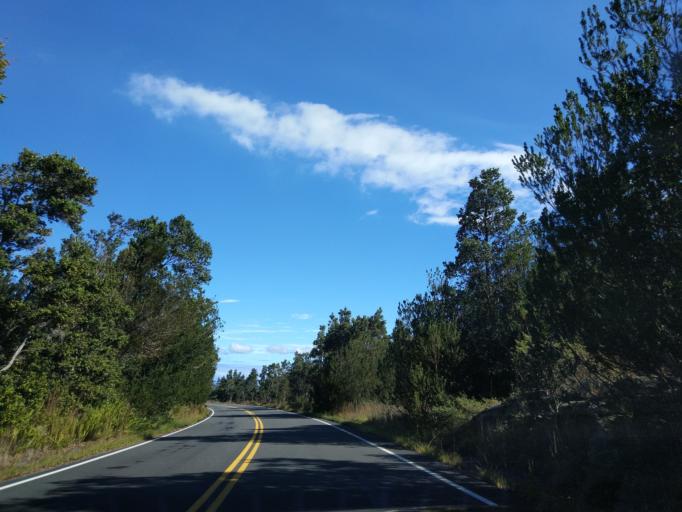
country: US
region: Hawaii
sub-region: Hawaii County
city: Volcano
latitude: 19.3472
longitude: -155.2174
